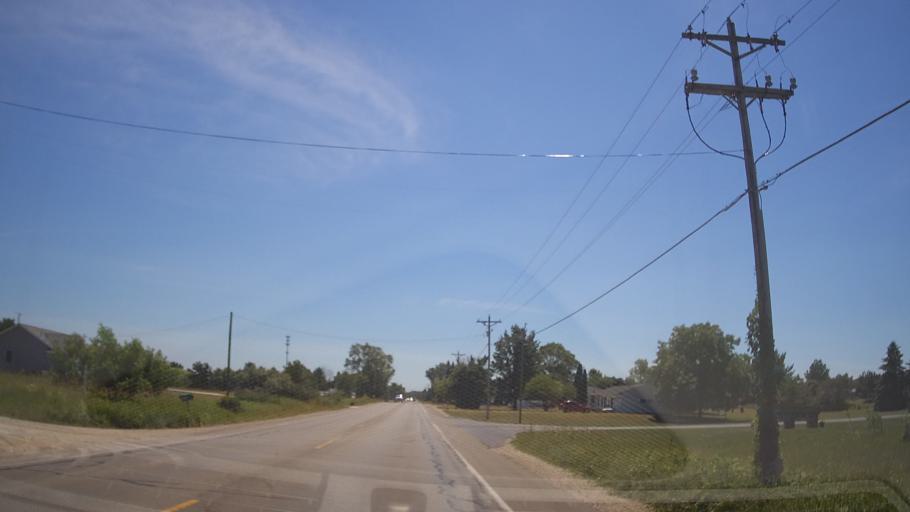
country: US
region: Michigan
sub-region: Grand Traverse County
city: Traverse City
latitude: 44.6779
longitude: -85.6898
